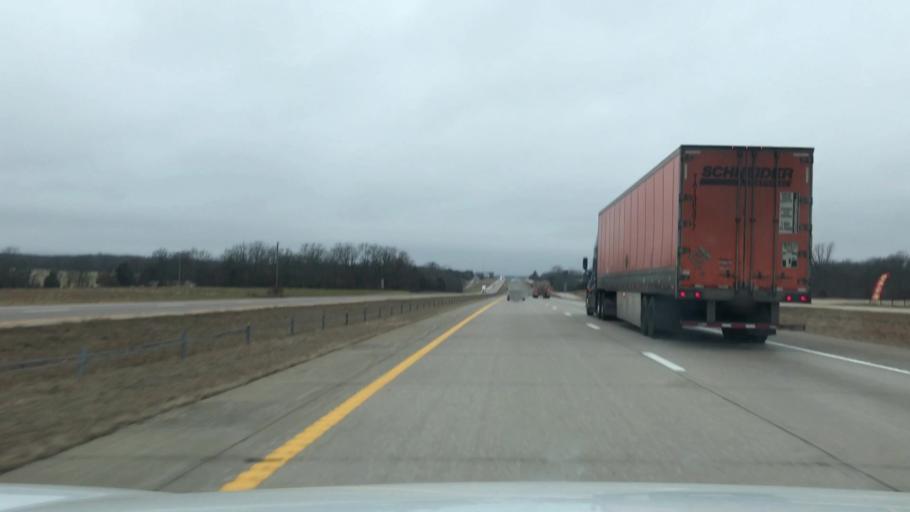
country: US
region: Missouri
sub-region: Crawford County
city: Bourbon
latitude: 38.1385
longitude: -91.2782
